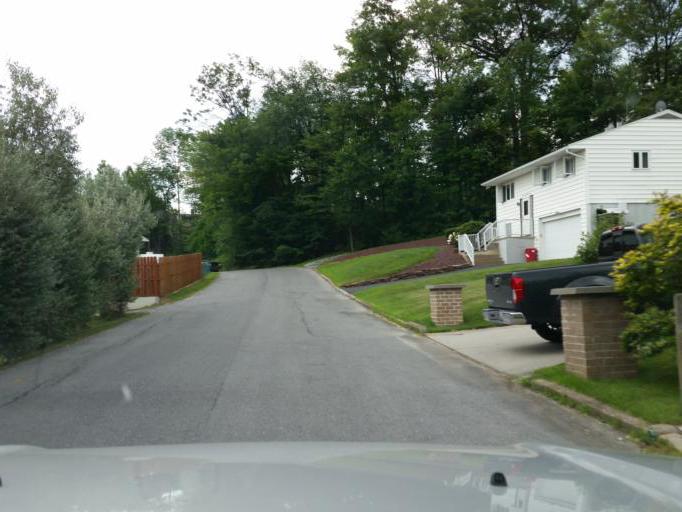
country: US
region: Pennsylvania
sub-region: Blair County
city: Altoona
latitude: 40.5343
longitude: -78.4080
